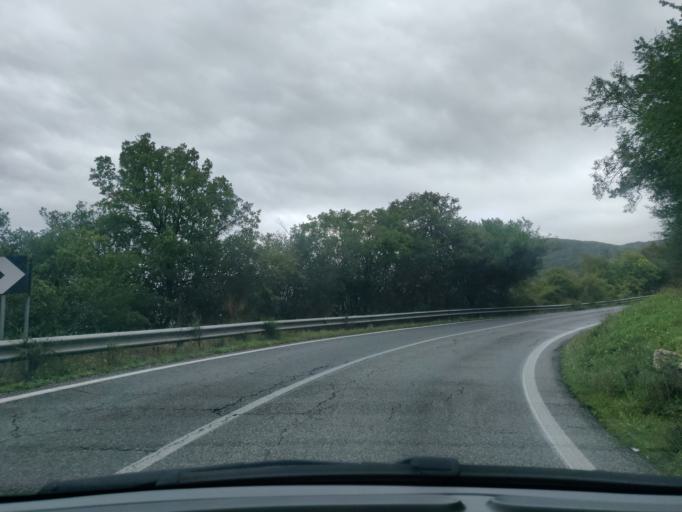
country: IT
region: Latium
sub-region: Citta metropolitana di Roma Capitale
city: Allumiere
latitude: 42.1451
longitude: 11.8886
